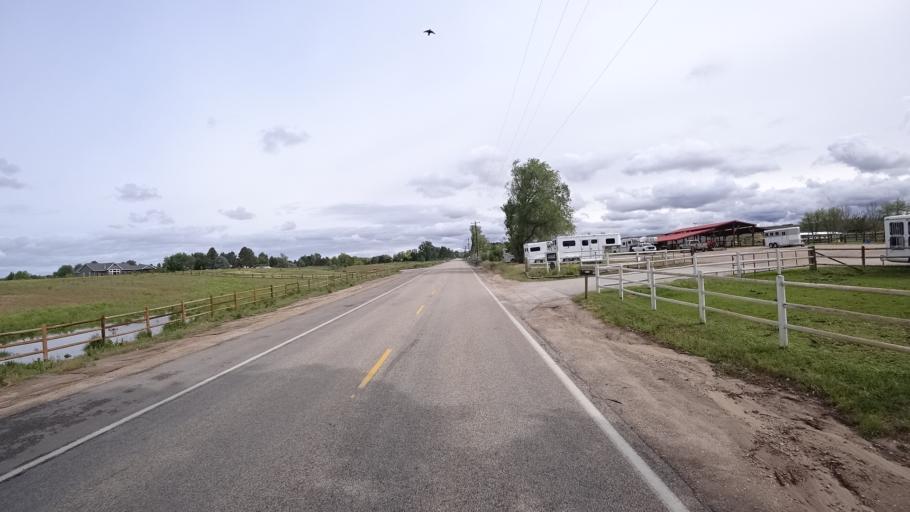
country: US
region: Idaho
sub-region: Ada County
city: Eagle
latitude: 43.7228
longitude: -116.3542
